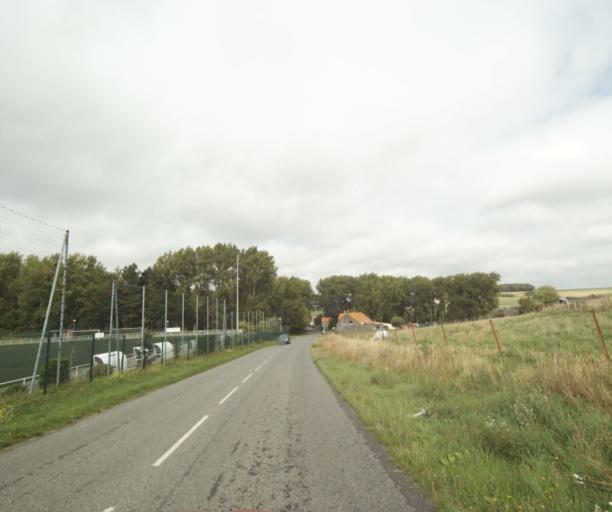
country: FR
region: Nord-Pas-de-Calais
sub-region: Departement du Pas-de-Calais
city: Etaples
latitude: 50.5203
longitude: 1.6534
